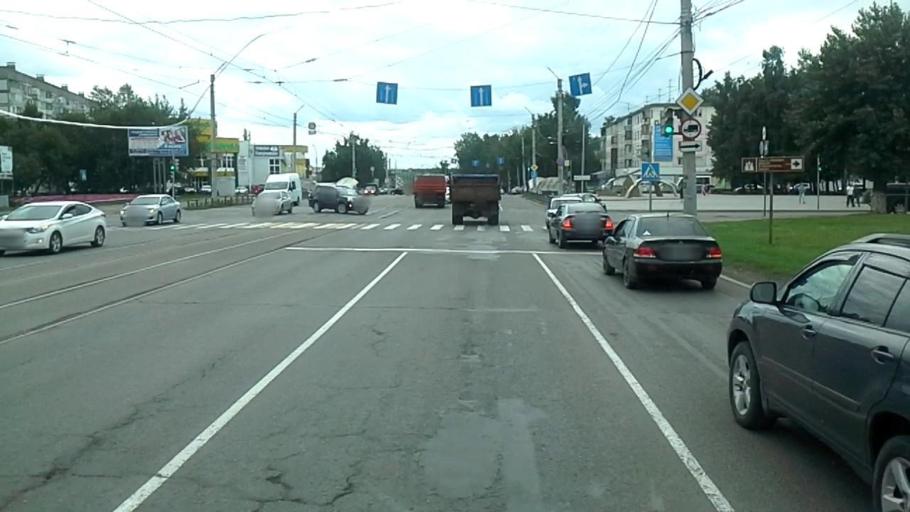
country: RU
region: Altai Krai
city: Biysk
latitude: 52.5420
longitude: 85.2189
